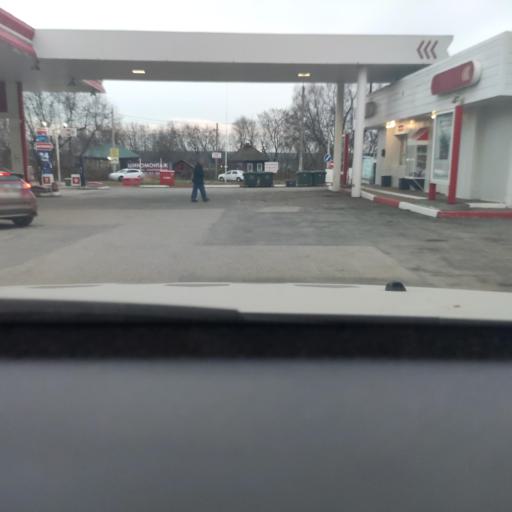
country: RU
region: Perm
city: Perm
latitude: 58.0291
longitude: 56.2961
